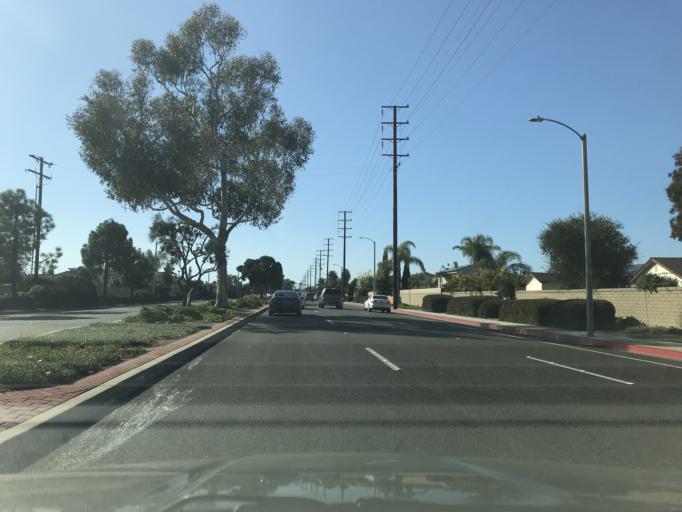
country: US
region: California
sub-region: Orange County
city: Huntington Beach
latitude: 33.6723
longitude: -117.9773
